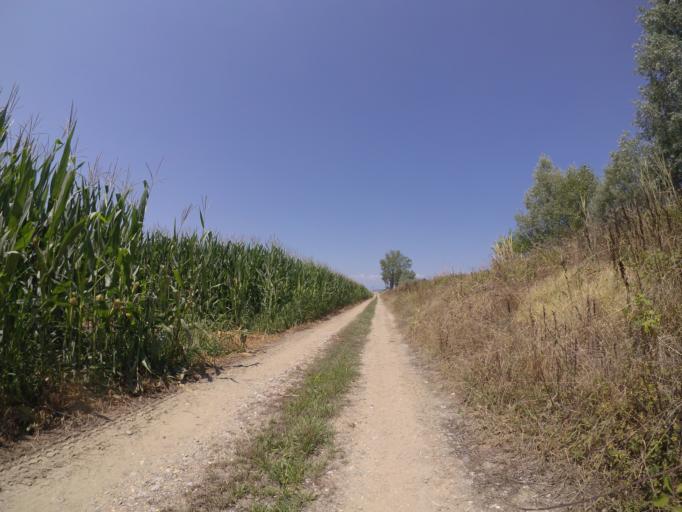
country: IT
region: Friuli Venezia Giulia
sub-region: Provincia di Udine
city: Codroipo
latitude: 45.9291
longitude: 13.0085
